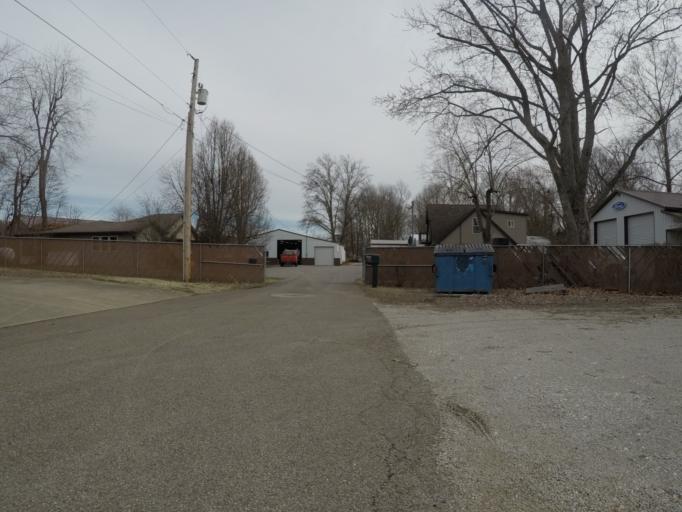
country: US
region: West Virginia
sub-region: Cabell County
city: Pea Ridge
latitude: 38.4491
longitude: -82.3457
